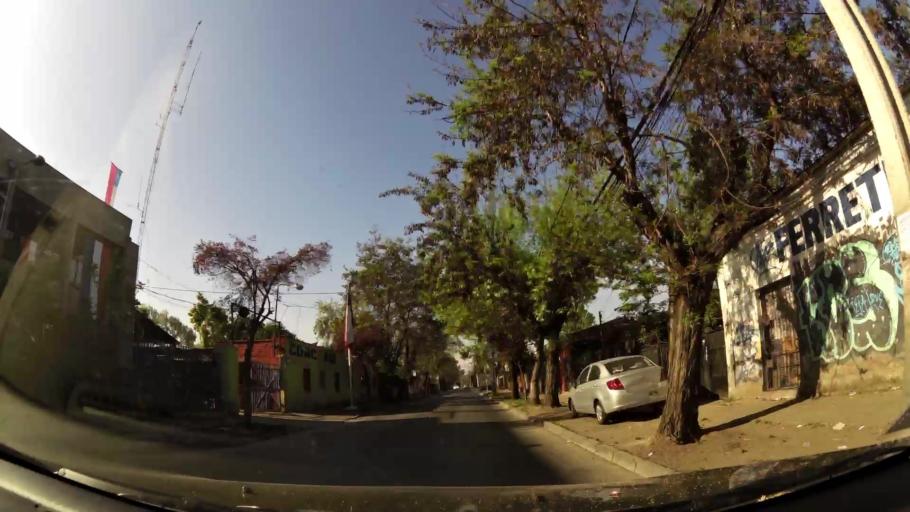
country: CL
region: Santiago Metropolitan
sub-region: Provincia de Santiago
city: Santiago
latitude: -33.3925
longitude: -70.6682
